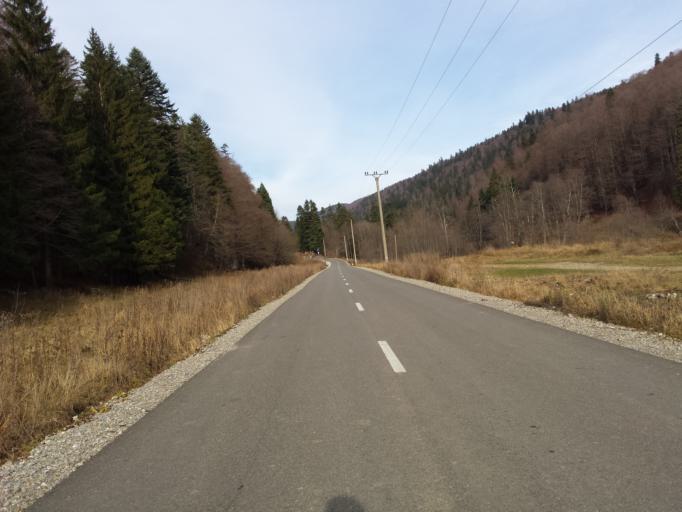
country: RO
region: Prahova
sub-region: Oras Azuga
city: Azuga
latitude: 45.4321
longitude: 25.5309
